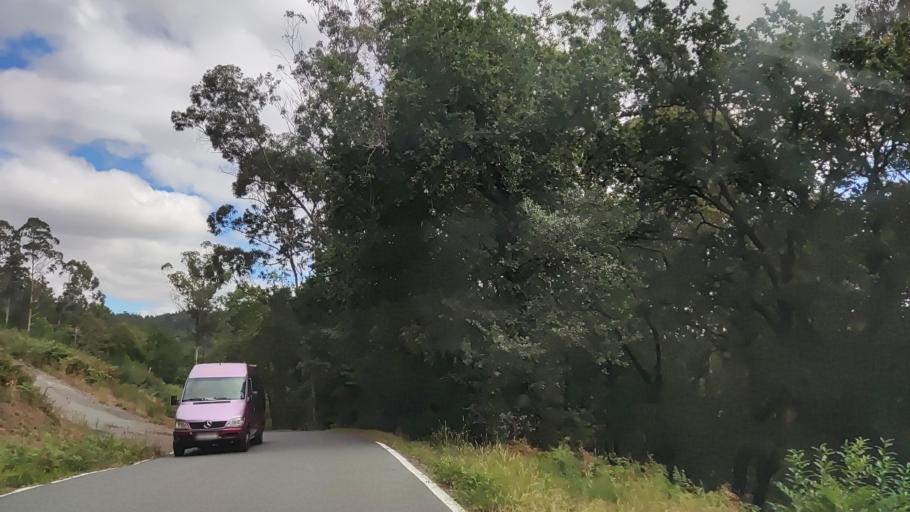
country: ES
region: Galicia
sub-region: Provincia da Coruna
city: Rois
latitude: 42.7358
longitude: -8.7022
